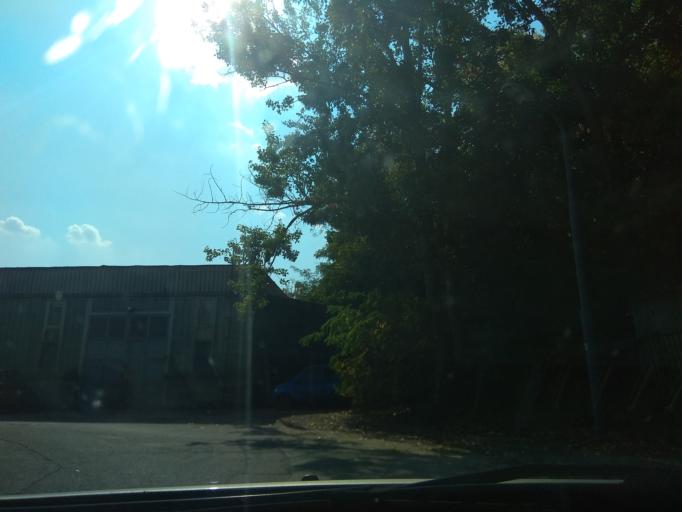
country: HU
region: Borsod-Abauj-Zemplen
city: Miskolc
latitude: 48.0805
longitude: 20.7618
